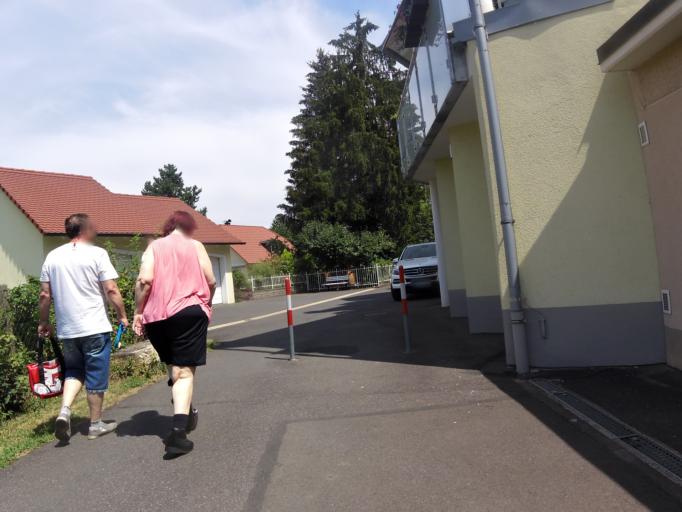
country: DE
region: Bavaria
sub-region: Regierungsbezirk Unterfranken
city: Estenfeld
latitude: 49.8107
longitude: 9.9861
